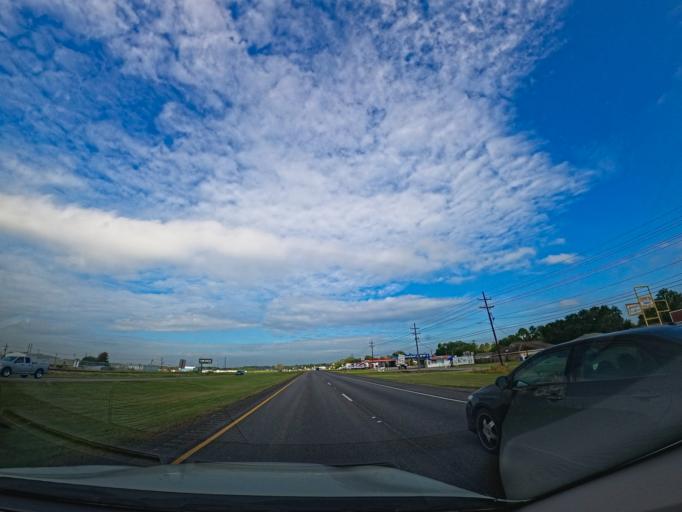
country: US
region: Louisiana
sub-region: Saint Mary Parish
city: Patterson
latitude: 29.6851
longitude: -91.3030
